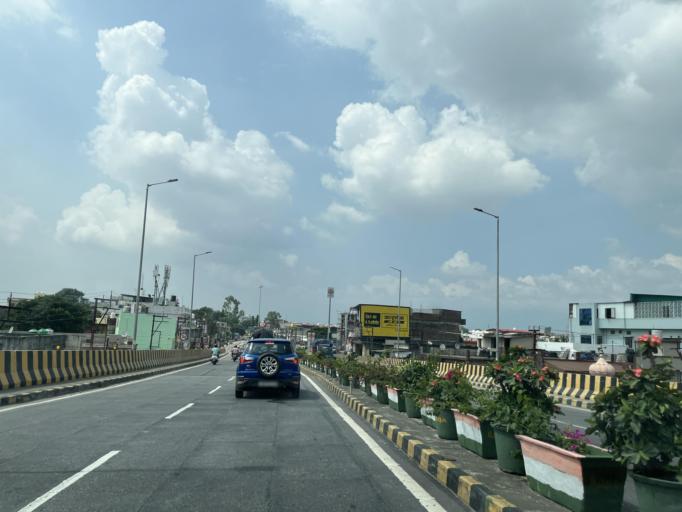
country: IN
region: Uttarakhand
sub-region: Dehradun
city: Raipur
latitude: 30.2783
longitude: 78.0737
